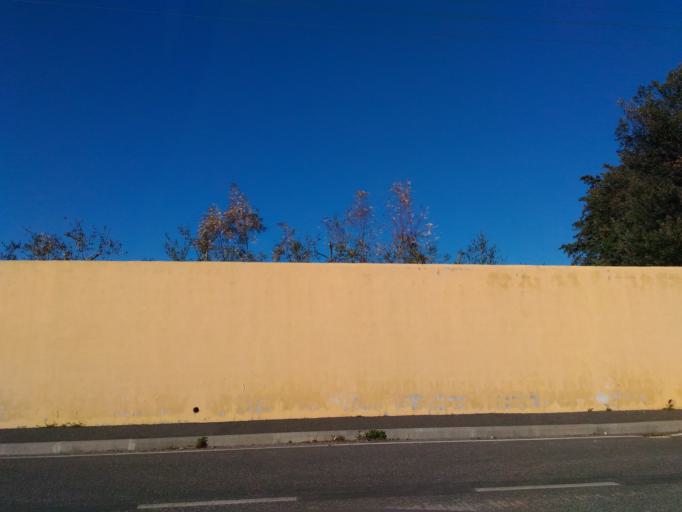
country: IT
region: Tuscany
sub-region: Provincia di Livorno
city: Livorno
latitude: 43.5032
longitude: 10.3338
